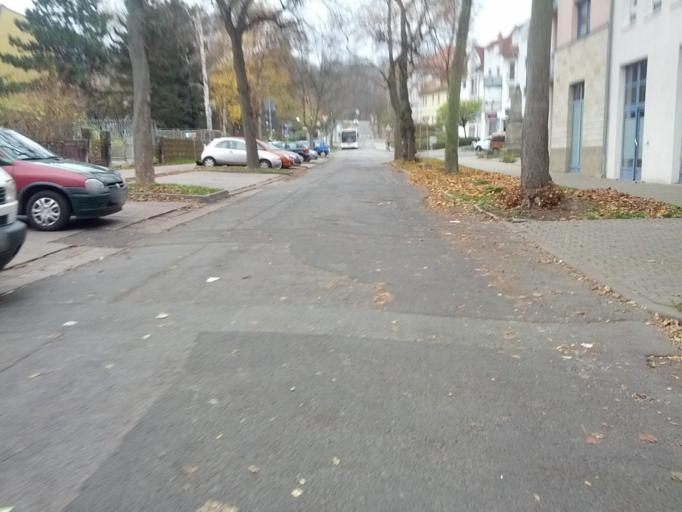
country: DE
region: Thuringia
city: Gotha
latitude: 50.9462
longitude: 10.6984
